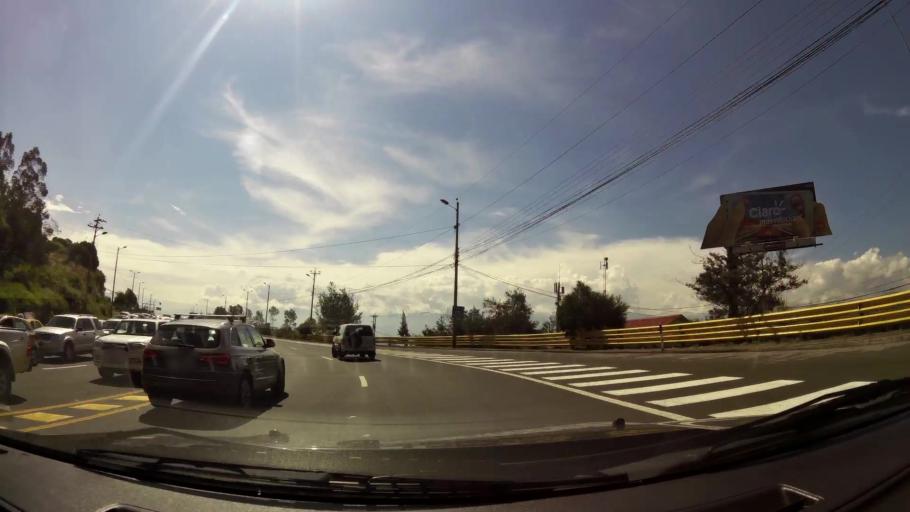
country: EC
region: Pichincha
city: Quito
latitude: -0.1915
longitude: -78.4556
